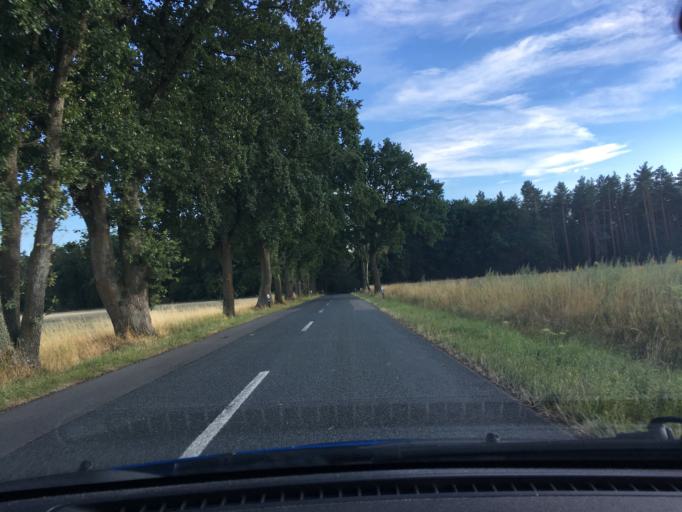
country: DE
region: Lower Saxony
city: Bleckede
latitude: 53.2548
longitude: 10.7095
